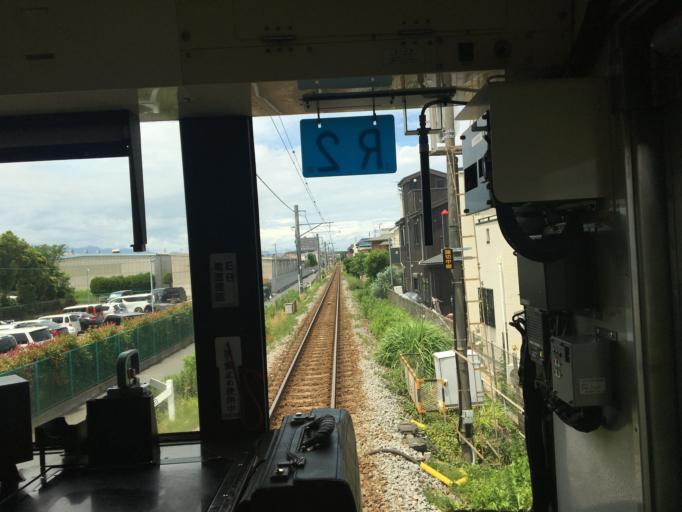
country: JP
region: Kanagawa
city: Chigasaki
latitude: 35.3423
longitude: 139.4059
